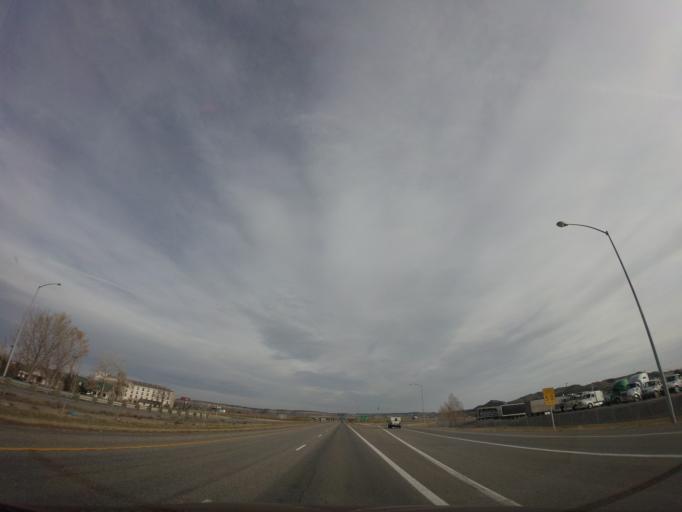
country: US
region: Montana
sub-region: Yellowstone County
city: Billings
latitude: 45.7521
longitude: -108.5396
